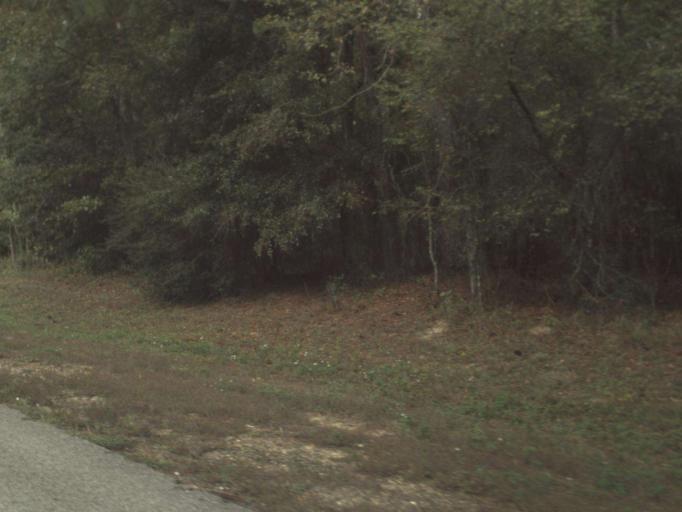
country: US
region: Florida
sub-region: Jackson County
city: Marianna
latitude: 30.6405
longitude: -85.1968
